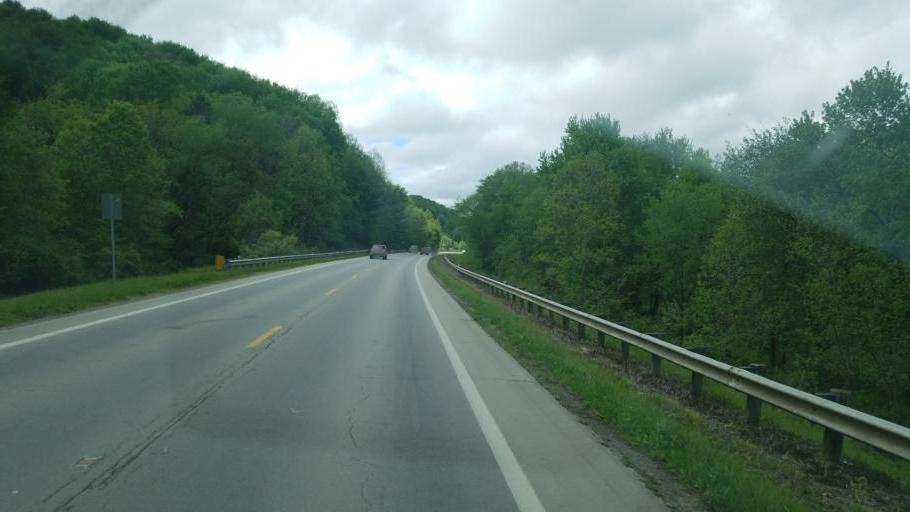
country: US
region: Ohio
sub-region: Tuscarawas County
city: Rockford
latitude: 40.4726
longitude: -81.3460
